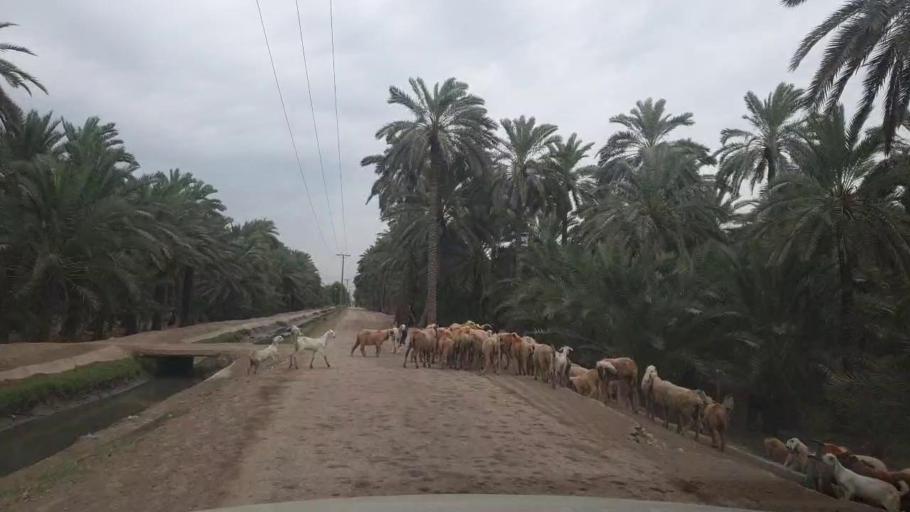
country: PK
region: Sindh
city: Sukkur
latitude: 27.6198
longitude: 68.8191
